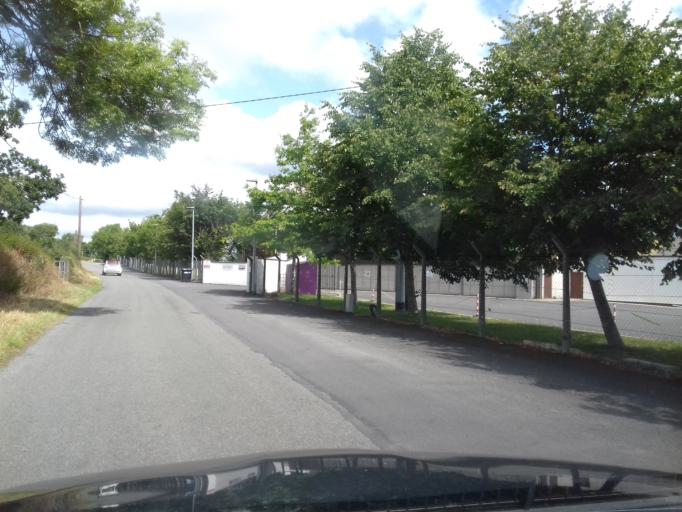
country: IE
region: Leinster
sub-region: Kilkenny
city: Graiguenamanagh
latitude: 52.5911
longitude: -6.9607
